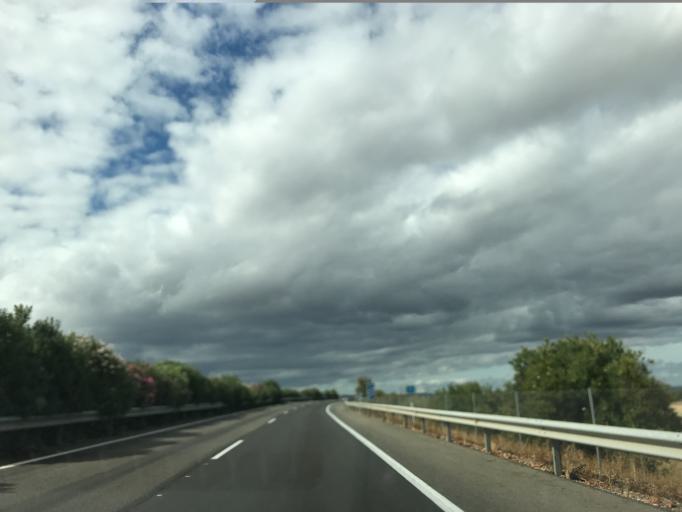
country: ES
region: Andalusia
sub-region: Province of Cordoba
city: Villa del Rio
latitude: 37.9873
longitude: -4.2735
